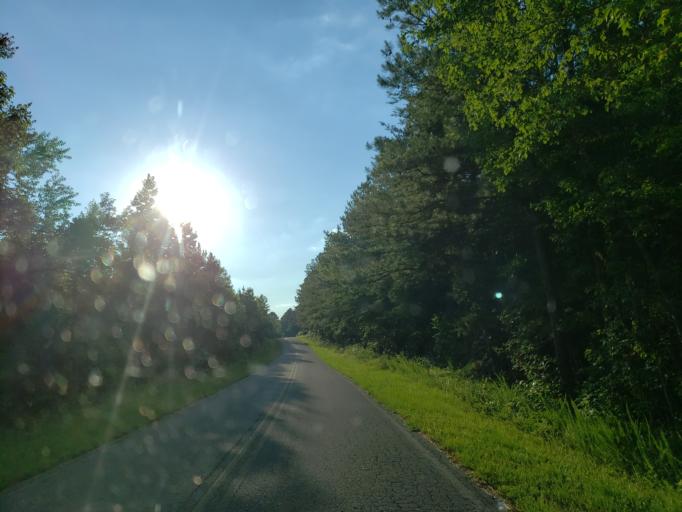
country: US
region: Georgia
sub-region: Haralson County
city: Tallapoosa
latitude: 33.8304
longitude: -85.2802
